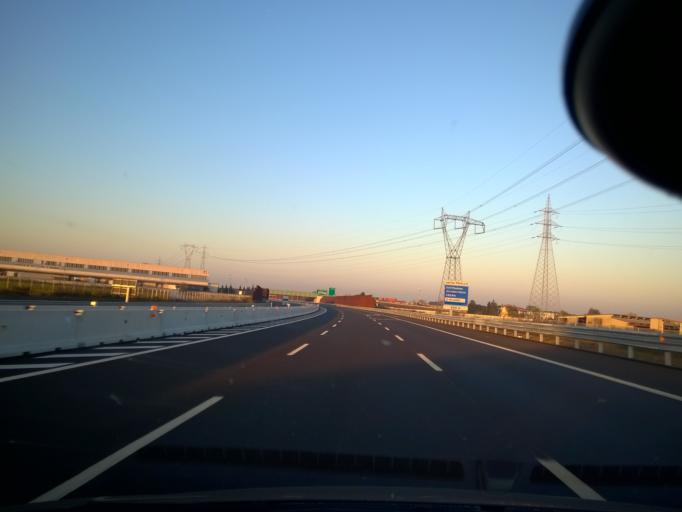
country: IT
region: Lombardy
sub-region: Provincia di Lodi
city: Zelo Buon Persico
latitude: 45.4141
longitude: 9.4162
